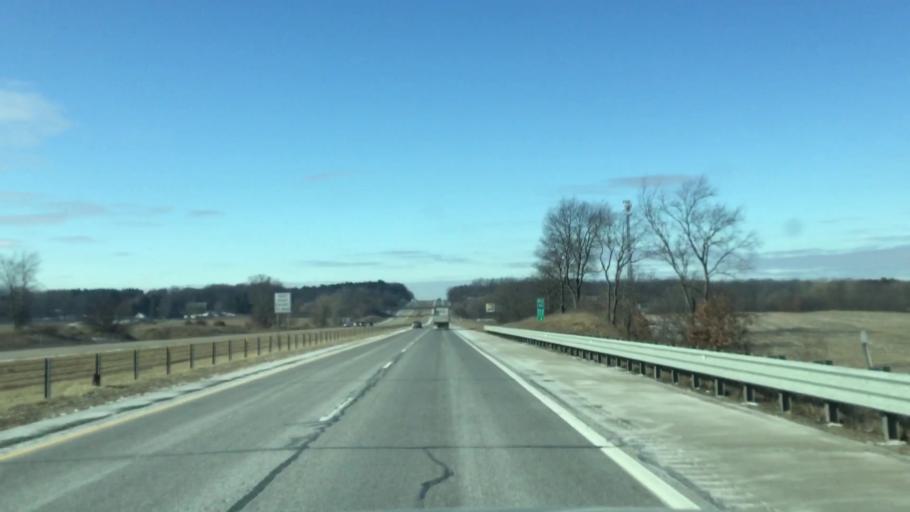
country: US
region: Michigan
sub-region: Calhoun County
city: Albion
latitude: 42.2838
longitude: -84.8193
